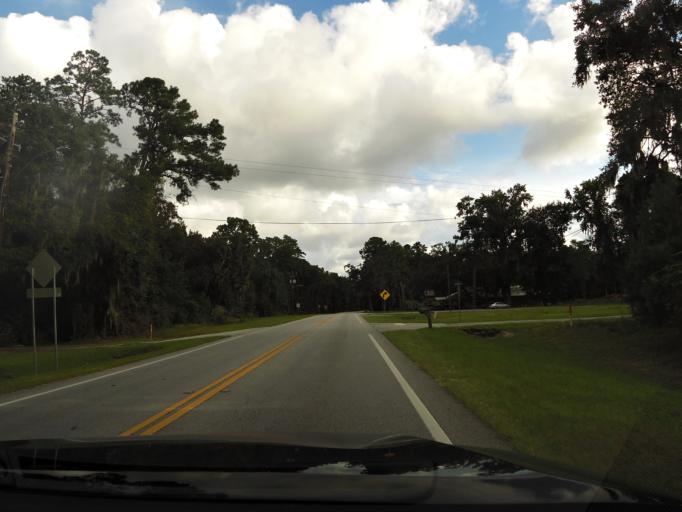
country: US
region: Georgia
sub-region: Liberty County
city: Midway
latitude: 31.7966
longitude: -81.4324
